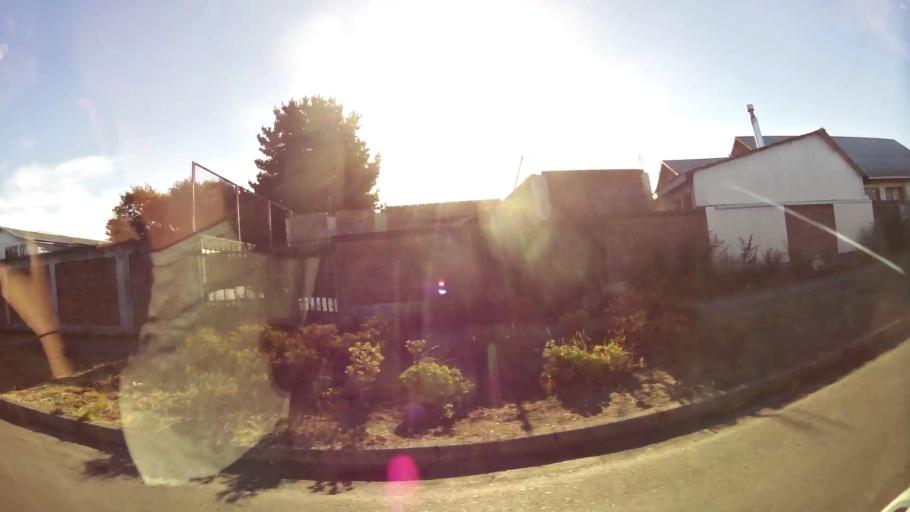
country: CL
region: Biobio
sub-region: Provincia de Concepcion
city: Concepcion
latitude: -36.8295
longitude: -73.1185
